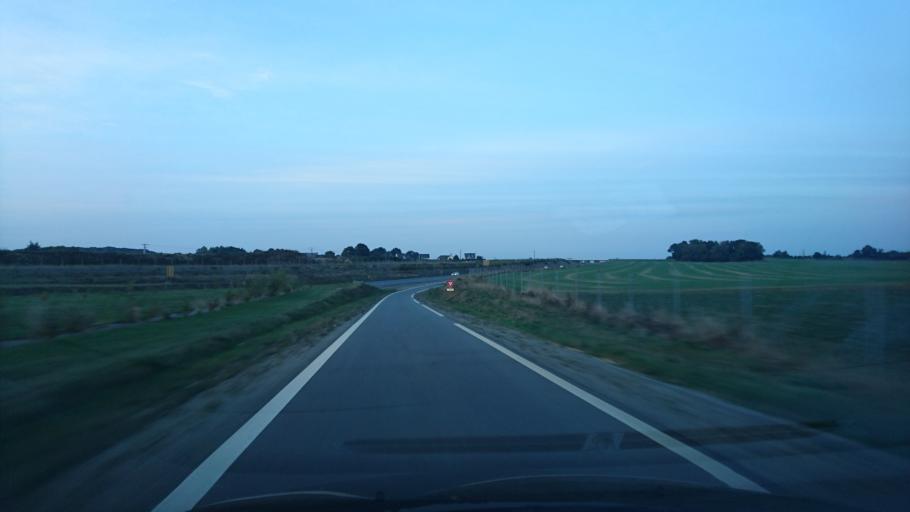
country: FR
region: Brittany
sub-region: Departement d'Ille-et-Vilaine
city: Guignen
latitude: 47.9216
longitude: -1.8512
